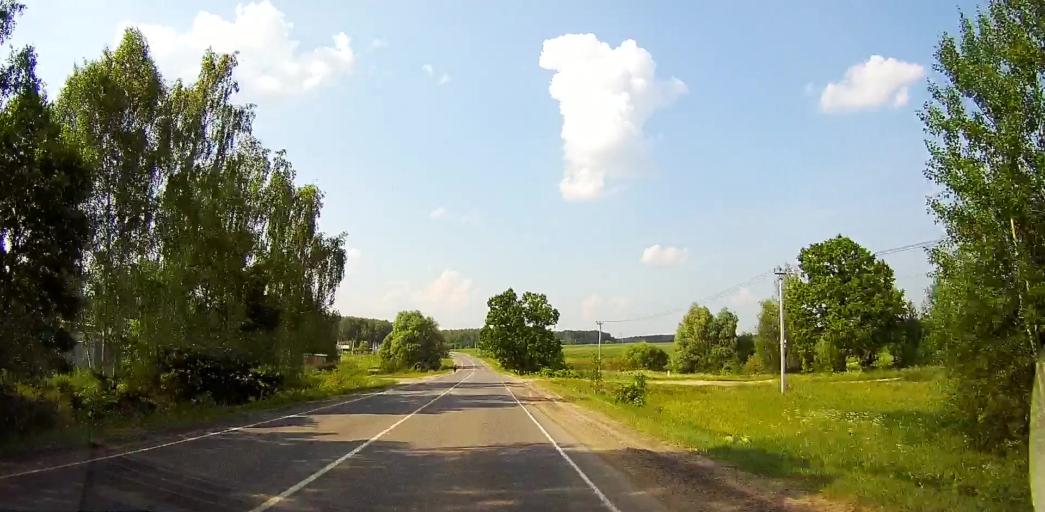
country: RU
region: Moskovskaya
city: Il'inskoye
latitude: 55.2041
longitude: 37.9626
